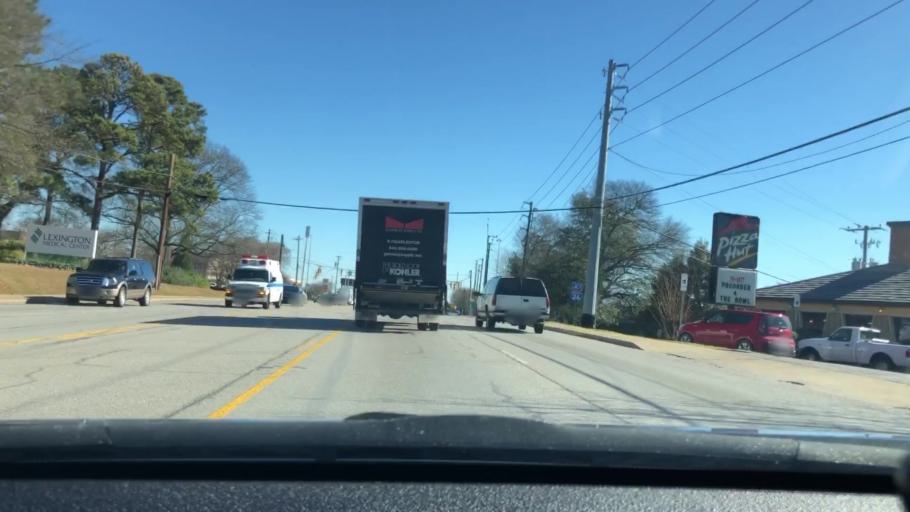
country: US
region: South Carolina
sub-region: Lexington County
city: Oak Grove
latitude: 34.0044
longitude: -81.1142
